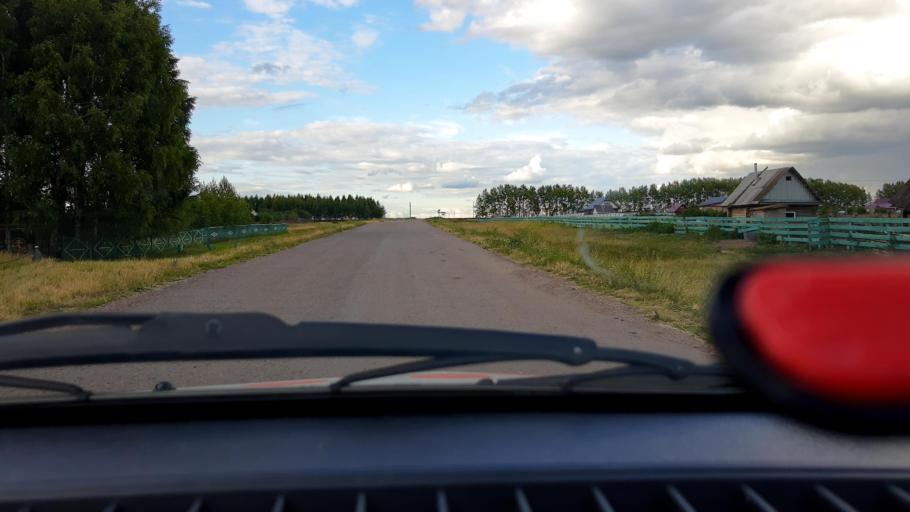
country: RU
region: Bashkortostan
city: Karmaskaly
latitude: 54.4240
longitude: 56.0275
